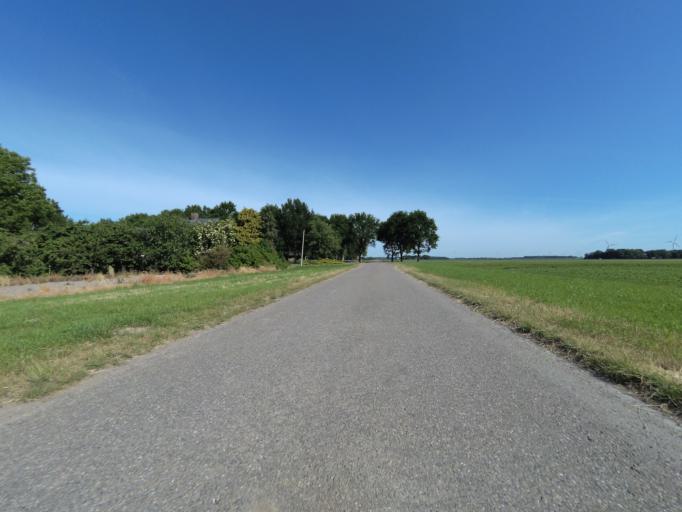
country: NL
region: Utrecht
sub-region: Gemeente Bunschoten
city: Bunschoten
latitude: 52.2960
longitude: 5.4169
